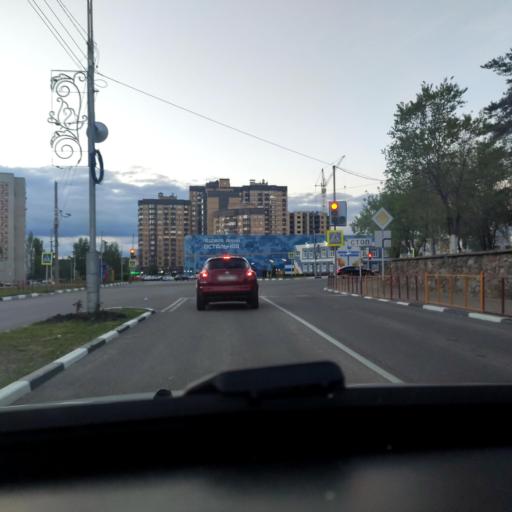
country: RU
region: Voronezj
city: Novovoronezh
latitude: 51.3162
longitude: 39.2073
